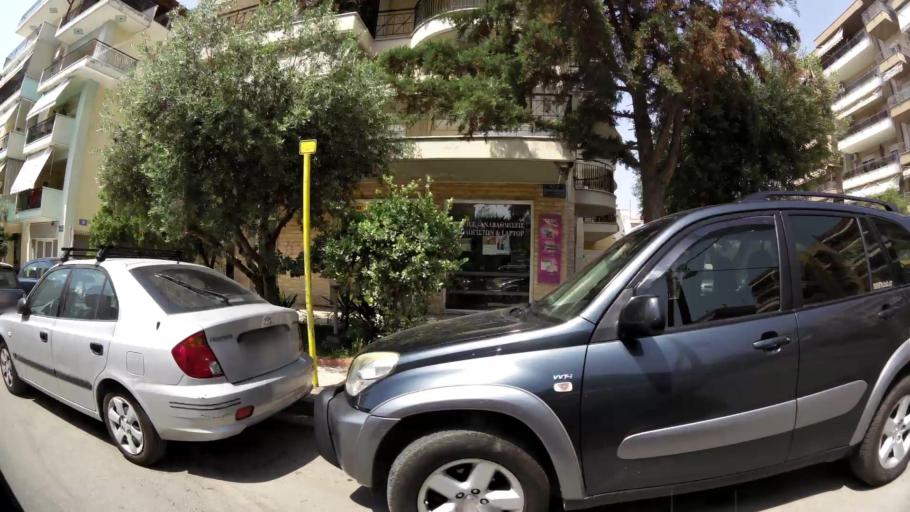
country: GR
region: Central Macedonia
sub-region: Nomos Thessalonikis
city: Evosmos
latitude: 40.6728
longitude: 22.9132
